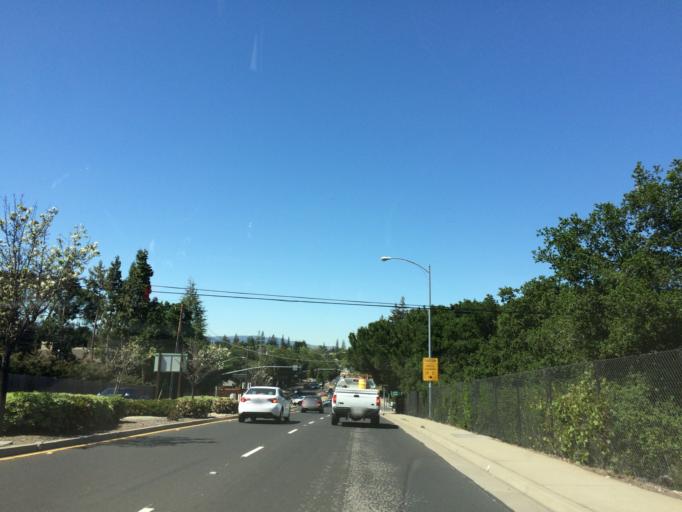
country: US
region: California
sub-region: Santa Clara County
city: Los Gatos
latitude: 37.2499
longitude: -121.9600
